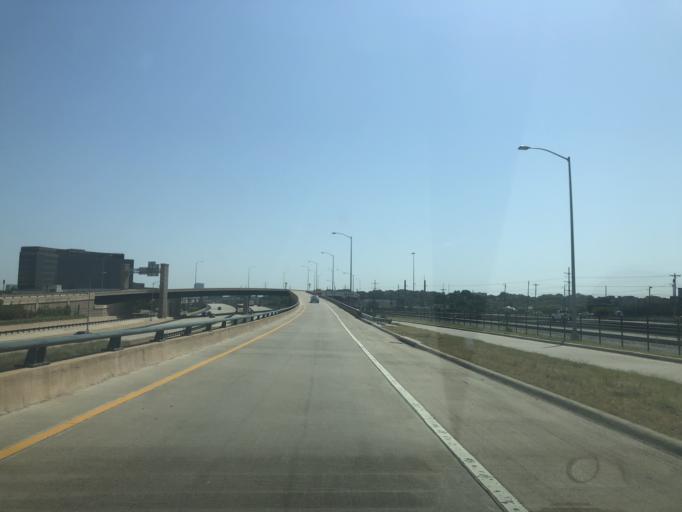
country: US
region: Texas
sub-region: Tarrant County
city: Fort Worth
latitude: 32.7295
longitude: -97.3673
